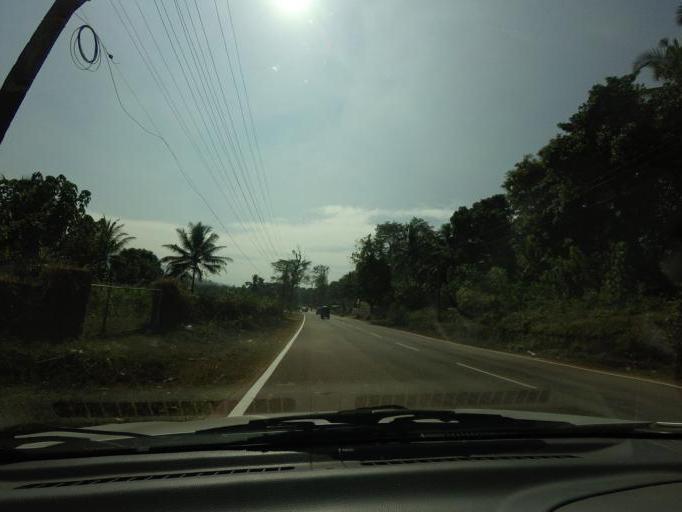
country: IN
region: Karnataka
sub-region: Dakshina Kannada
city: Sulya
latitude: 12.6849
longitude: 75.6088
